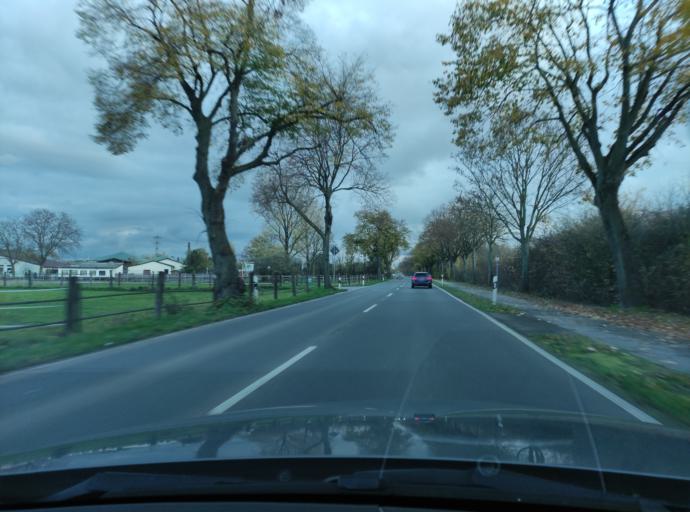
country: DE
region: North Rhine-Westphalia
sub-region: Regierungsbezirk Dusseldorf
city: Dormagen
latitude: 51.1058
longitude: 6.7883
